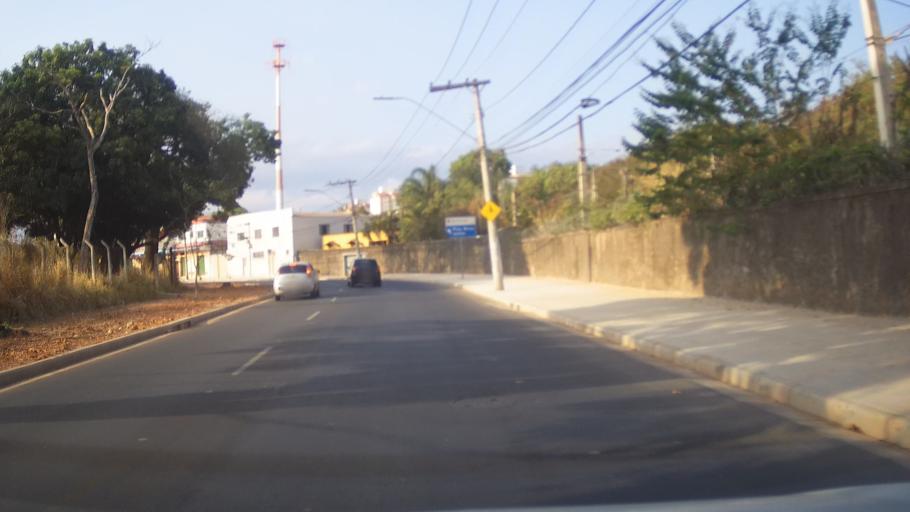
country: BR
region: Minas Gerais
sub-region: Belo Horizonte
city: Belo Horizonte
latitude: -19.8882
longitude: -43.9123
